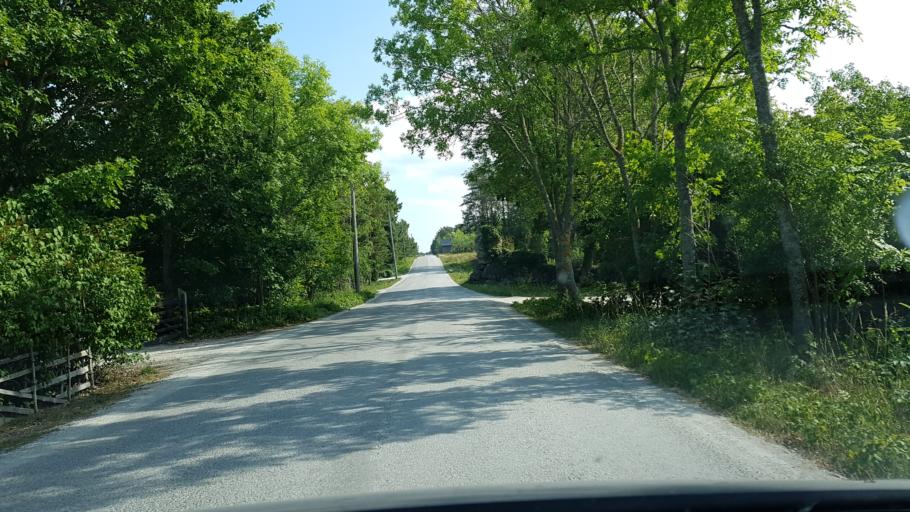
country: SE
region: Gotland
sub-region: Gotland
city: Visby
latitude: 57.8230
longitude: 18.5156
